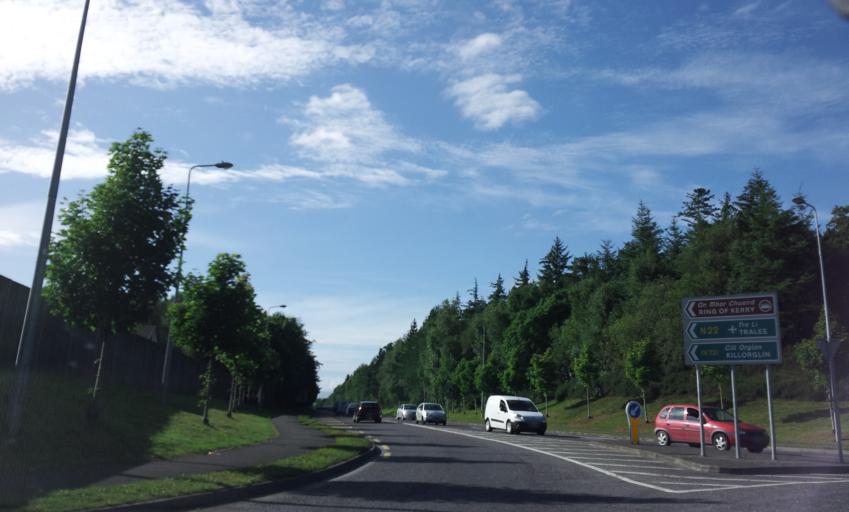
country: IE
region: Munster
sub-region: Ciarrai
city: Cill Airne
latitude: 52.0628
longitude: -9.4858
